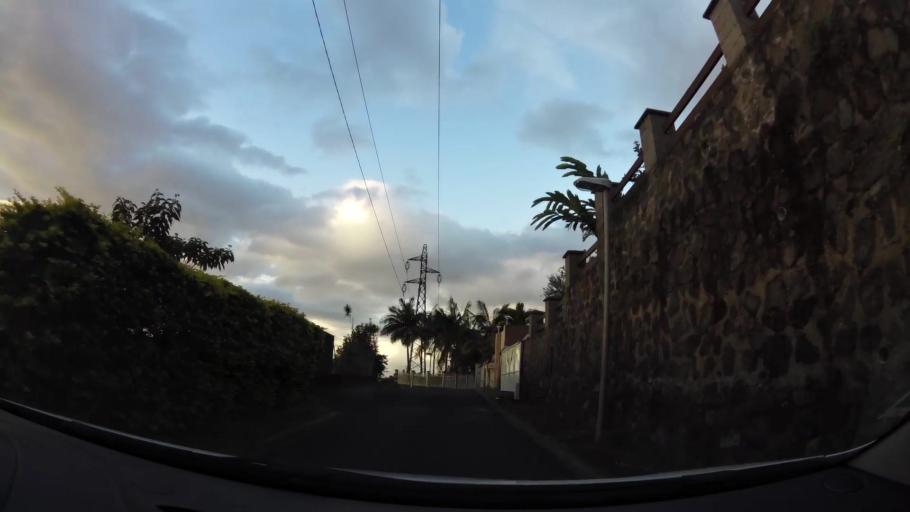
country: RE
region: Reunion
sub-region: Reunion
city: Saint-Denis
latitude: -20.9193
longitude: 55.4654
